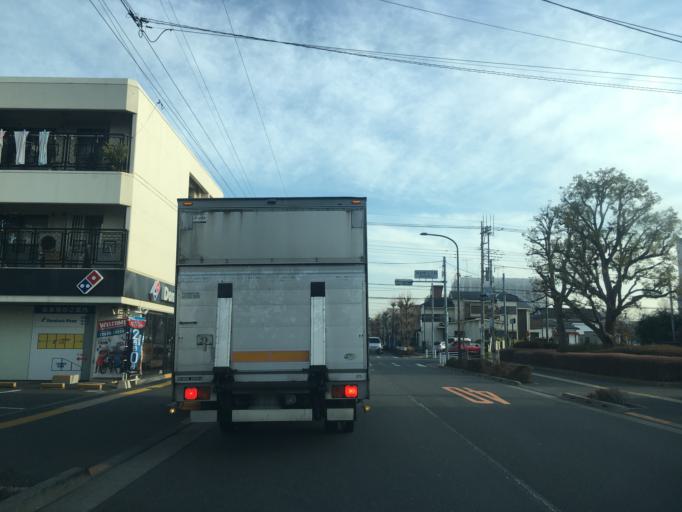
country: JP
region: Tokyo
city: Hino
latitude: 35.6903
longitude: 139.4235
